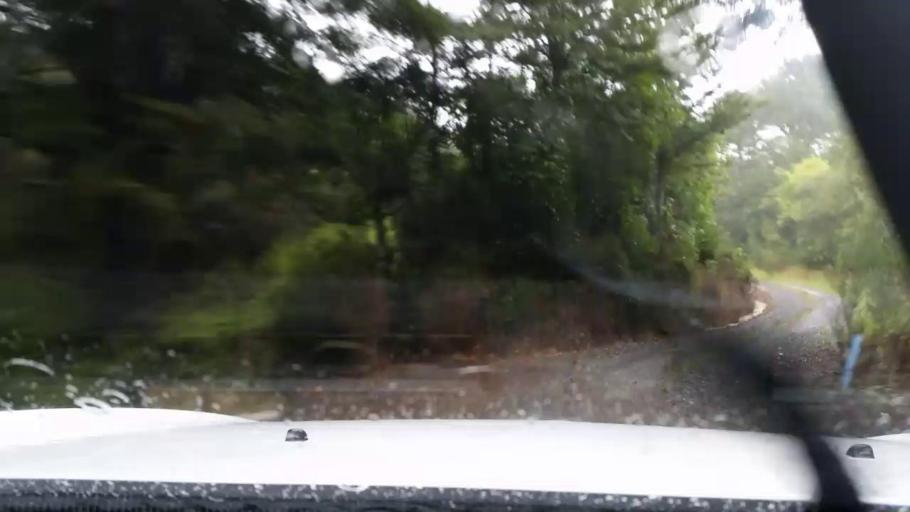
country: NZ
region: Wellington
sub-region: Masterton District
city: Masterton
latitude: -41.1599
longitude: 175.7983
